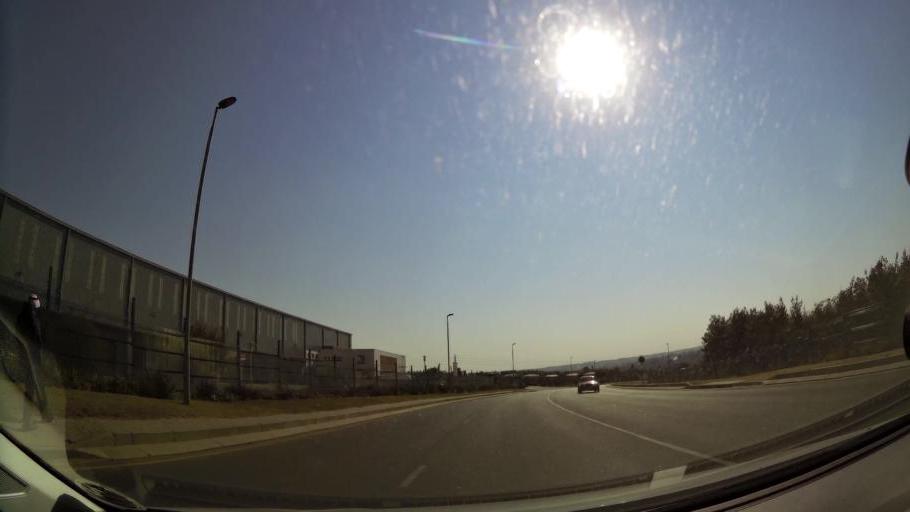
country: ZA
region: Gauteng
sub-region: City of Johannesburg Metropolitan Municipality
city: Modderfontein
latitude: -26.0980
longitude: 28.1403
